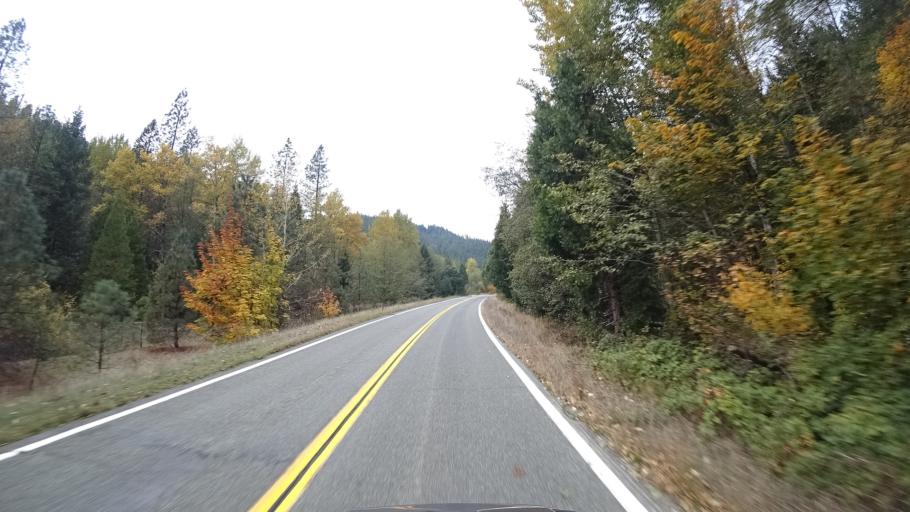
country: US
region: California
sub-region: Siskiyou County
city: Happy Camp
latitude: 41.9154
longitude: -123.4646
